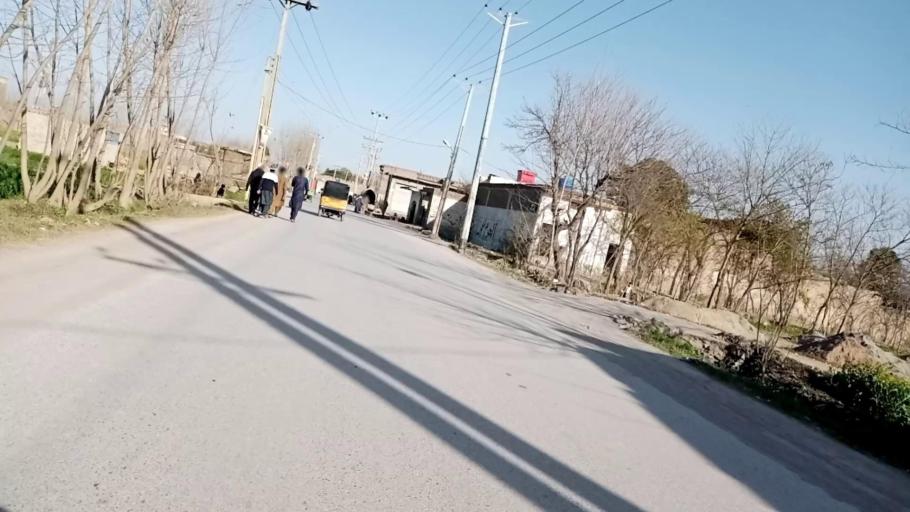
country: PK
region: Khyber Pakhtunkhwa
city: Peshawar
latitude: 34.0552
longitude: 71.5357
